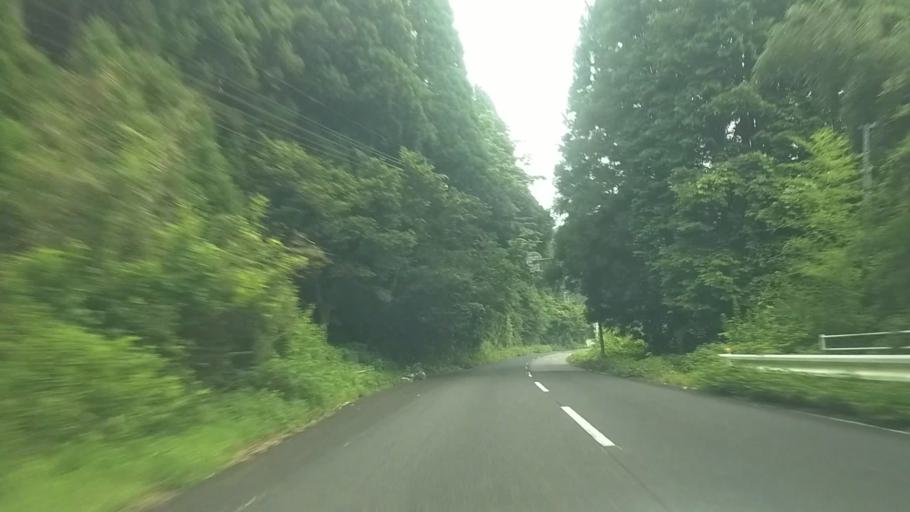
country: JP
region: Chiba
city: Katsuura
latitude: 35.2546
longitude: 140.2442
